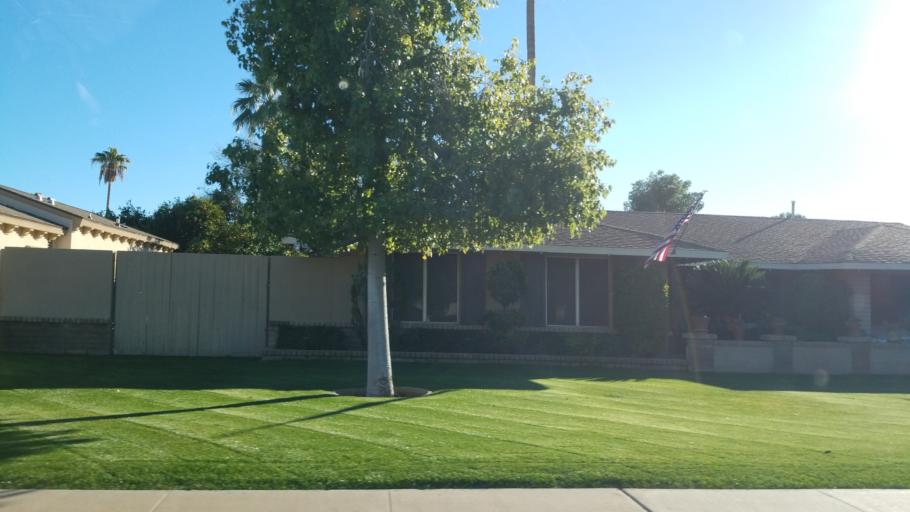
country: US
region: Arizona
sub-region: Maricopa County
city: Paradise Valley
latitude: 33.5942
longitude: -111.9752
